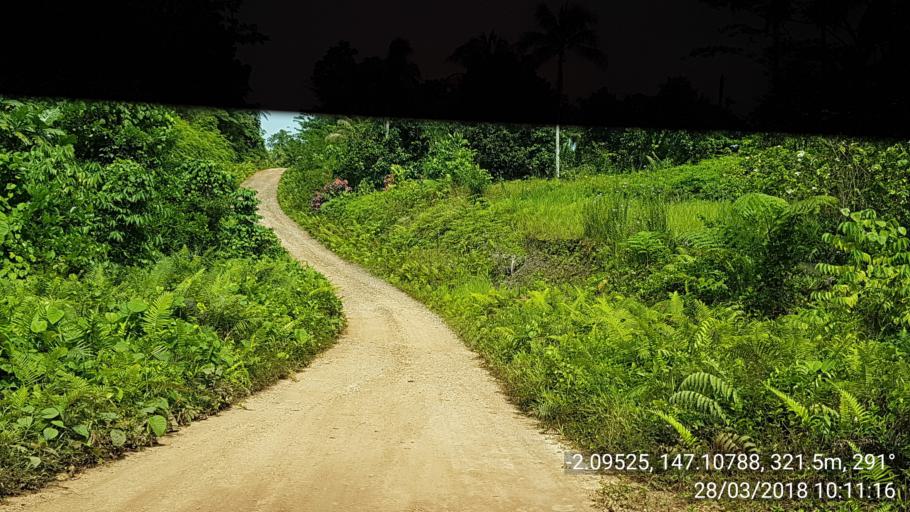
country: PG
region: Manus
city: Lorengau
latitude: -2.0953
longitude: 147.1077
